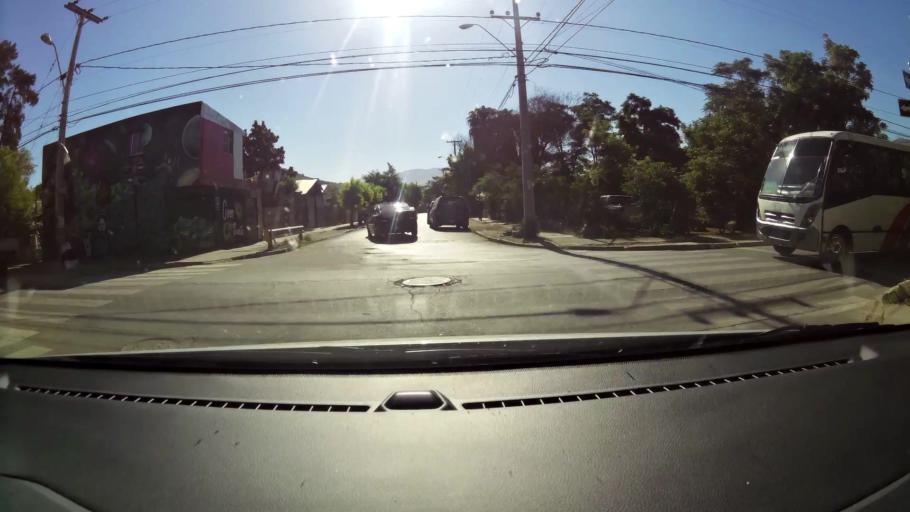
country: CL
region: Santiago Metropolitan
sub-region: Provincia de Chacabuco
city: Lampa
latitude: -33.4008
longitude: -71.1288
